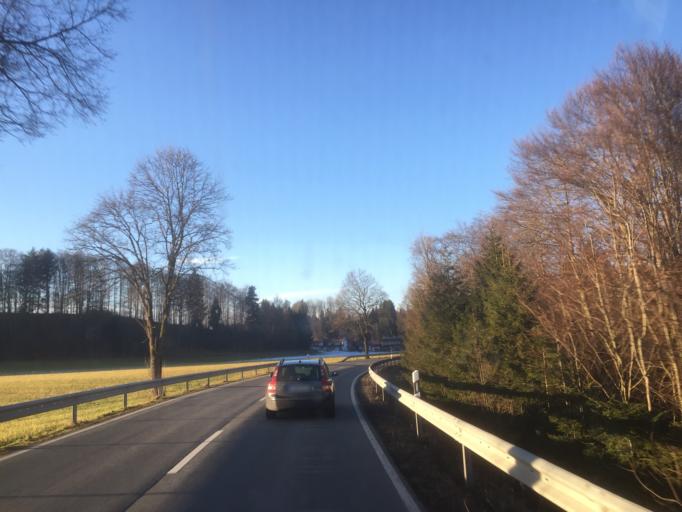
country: DE
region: Bavaria
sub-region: Upper Bavaria
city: Vachendorf
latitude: 47.8405
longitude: 12.6339
